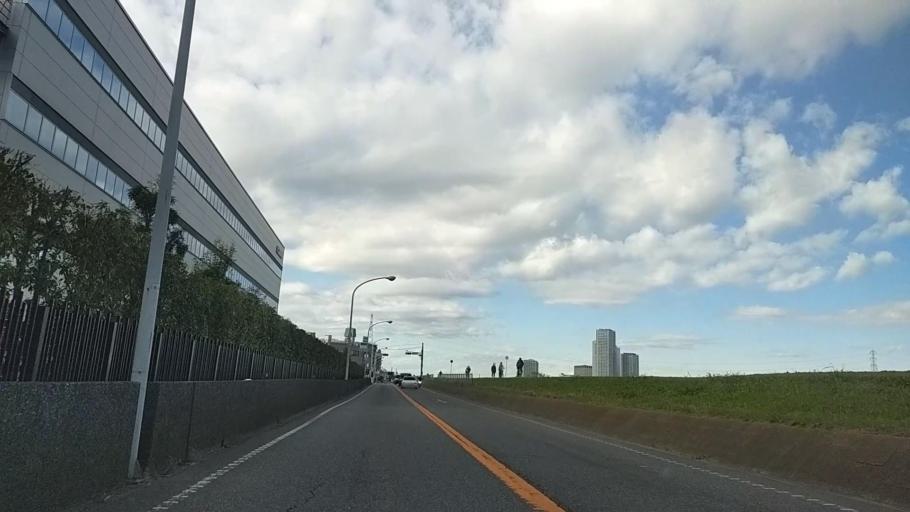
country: JP
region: Tokyo
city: Tokyo
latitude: 35.5962
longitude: 139.6417
